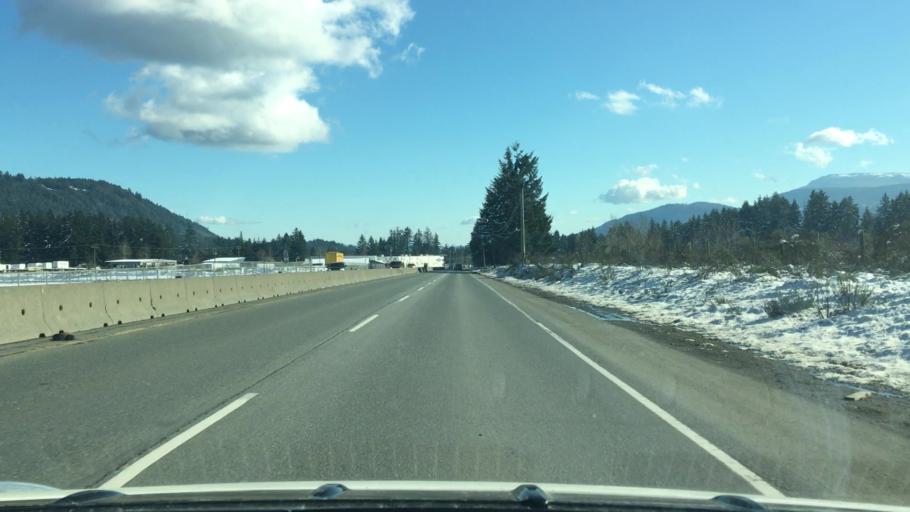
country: CA
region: British Columbia
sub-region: Cowichan Valley Regional District
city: Ladysmith
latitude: 49.0420
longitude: -123.8695
